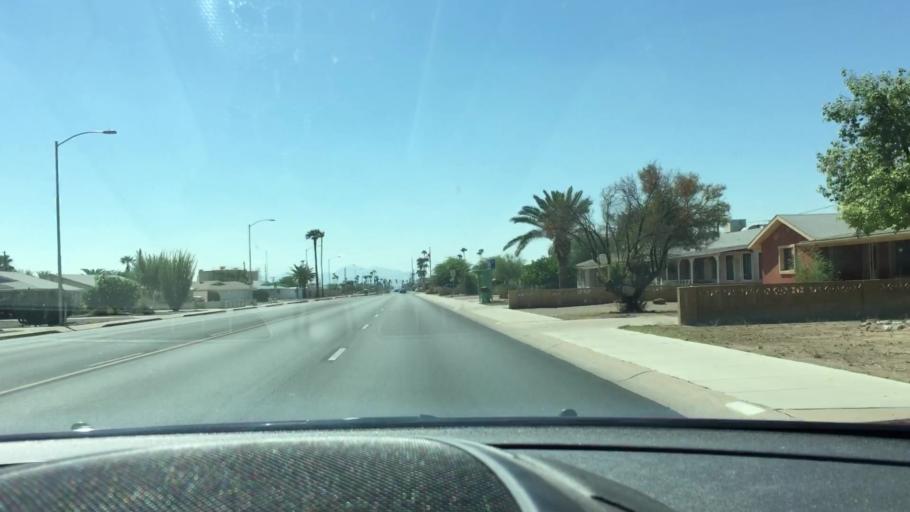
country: US
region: Arizona
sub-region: Maricopa County
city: Youngtown
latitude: 33.5994
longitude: -112.2988
